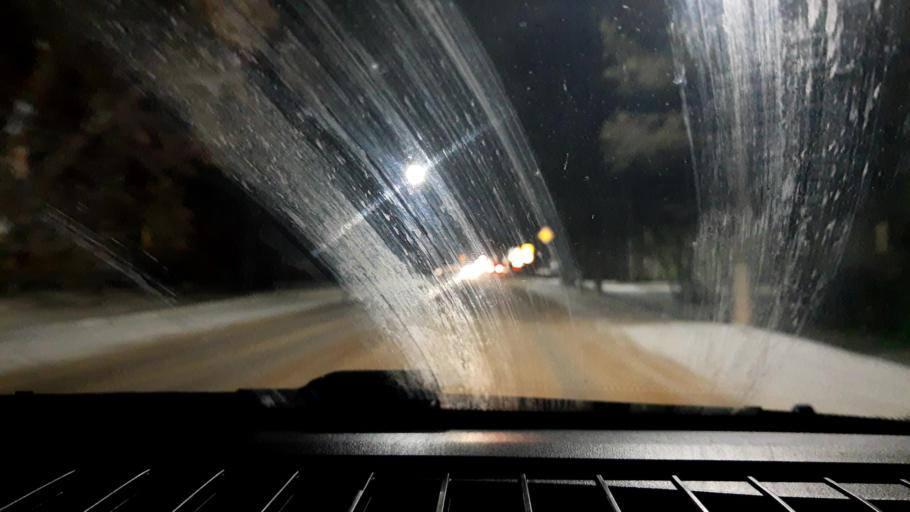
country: RU
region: Nizjnij Novgorod
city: Bogorodsk
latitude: 56.0957
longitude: 43.5368
